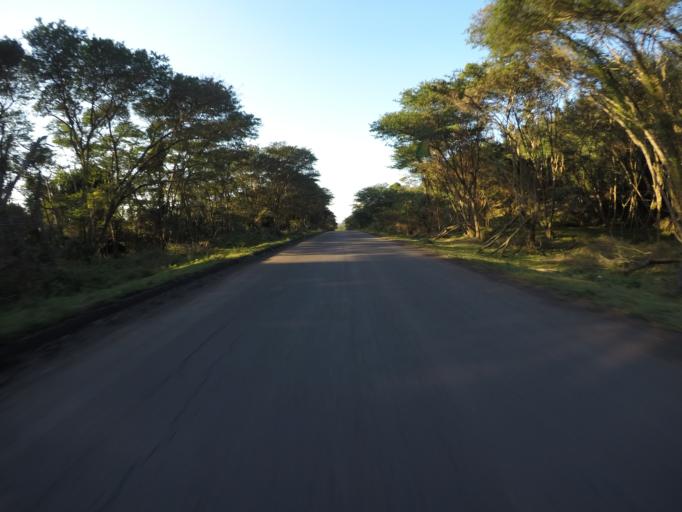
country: ZA
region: KwaZulu-Natal
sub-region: uThungulu District Municipality
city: KwaMbonambi
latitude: -28.6974
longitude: 32.2080
